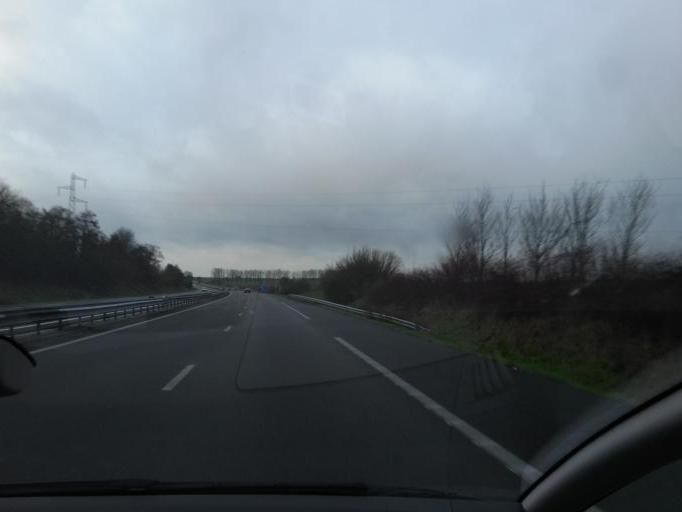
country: FR
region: Picardie
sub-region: Departement de la Somme
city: Moislains
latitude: 50.0349
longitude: 2.9030
